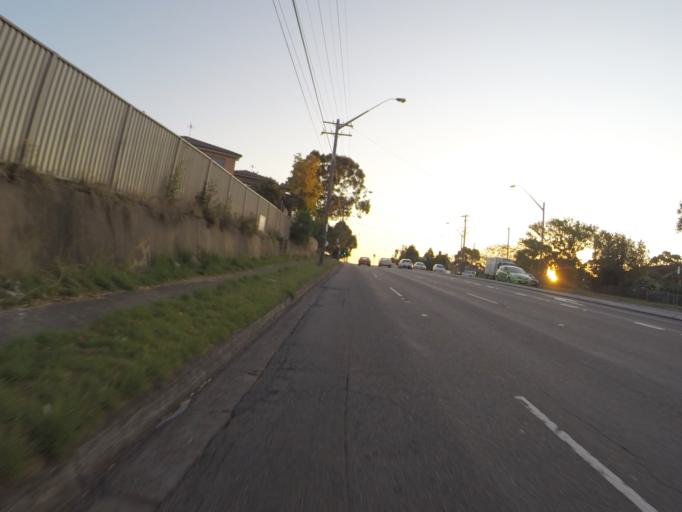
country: AU
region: New South Wales
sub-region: Bankstown
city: Padstow
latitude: -33.9662
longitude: 151.0366
